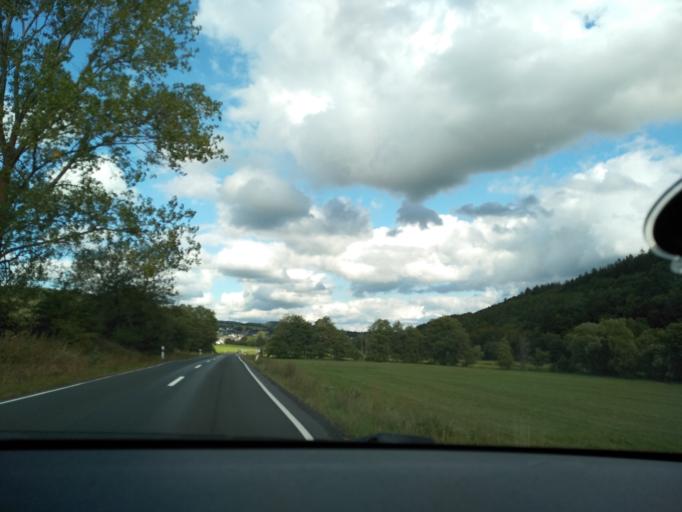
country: DE
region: Hesse
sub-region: Regierungsbezirk Giessen
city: Haiger
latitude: 50.7451
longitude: 8.1636
